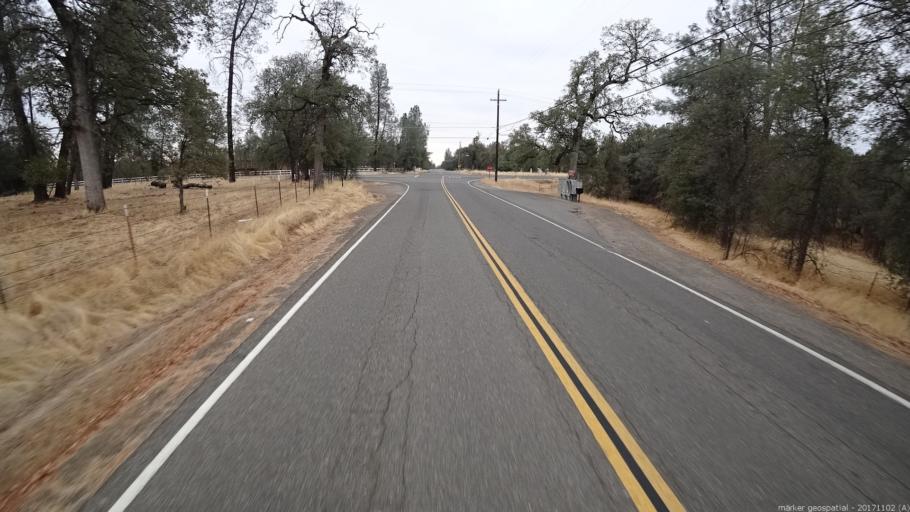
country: US
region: California
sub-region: Shasta County
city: Bella Vista
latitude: 40.6264
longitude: -122.2967
